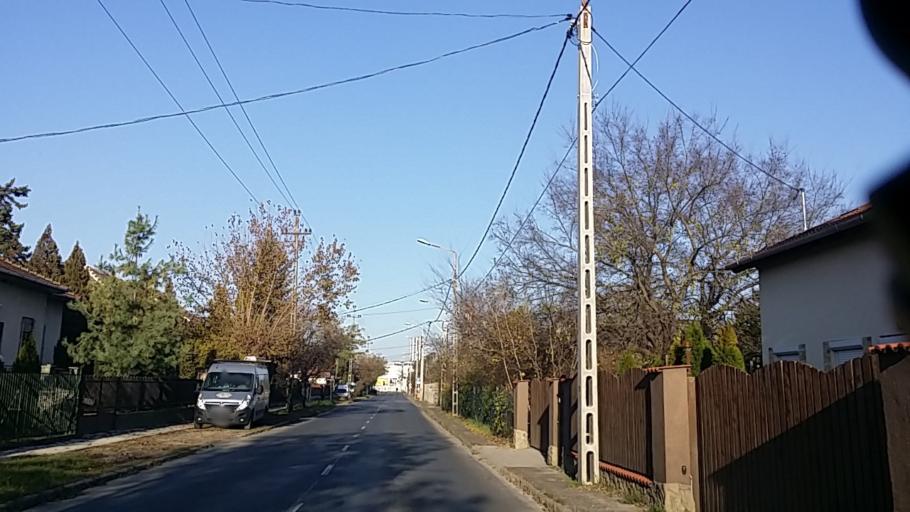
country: HU
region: Budapest
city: Budapest XVII. keruelet
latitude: 47.4752
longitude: 19.2431
